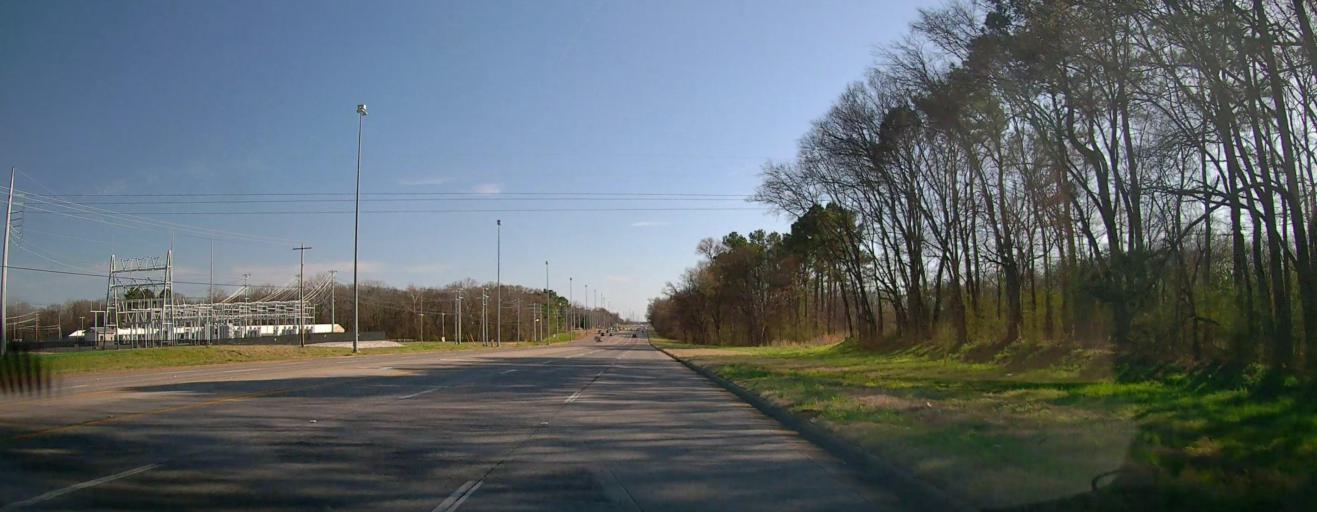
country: US
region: Alabama
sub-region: Colbert County
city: Muscle Shoals
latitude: 34.7658
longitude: -87.6348
